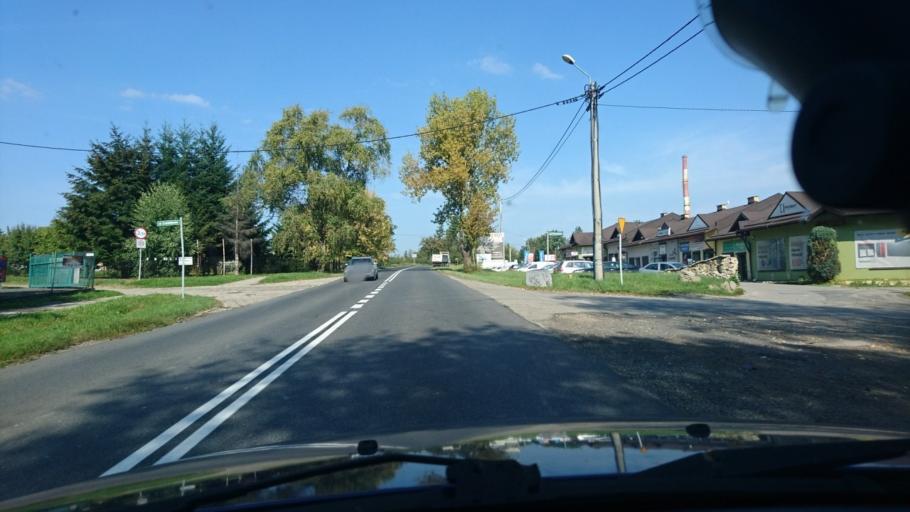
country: PL
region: Silesian Voivodeship
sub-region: Powiat bielski
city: Bestwina
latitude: 49.8631
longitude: 19.0309
